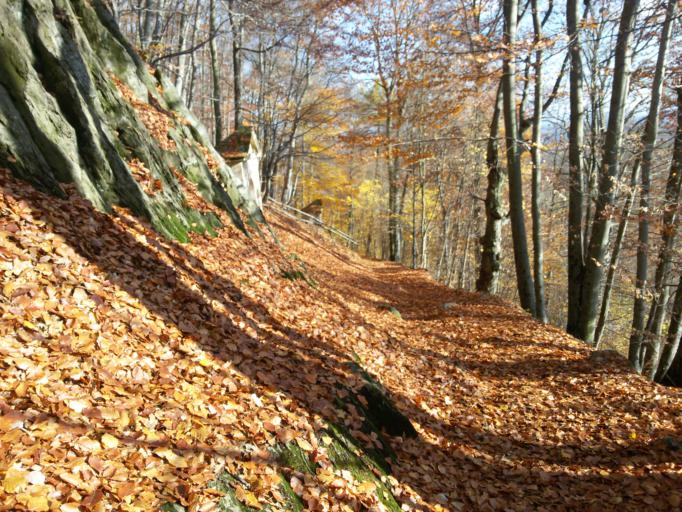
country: CZ
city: Doksy
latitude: 50.5382
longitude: 14.7209
